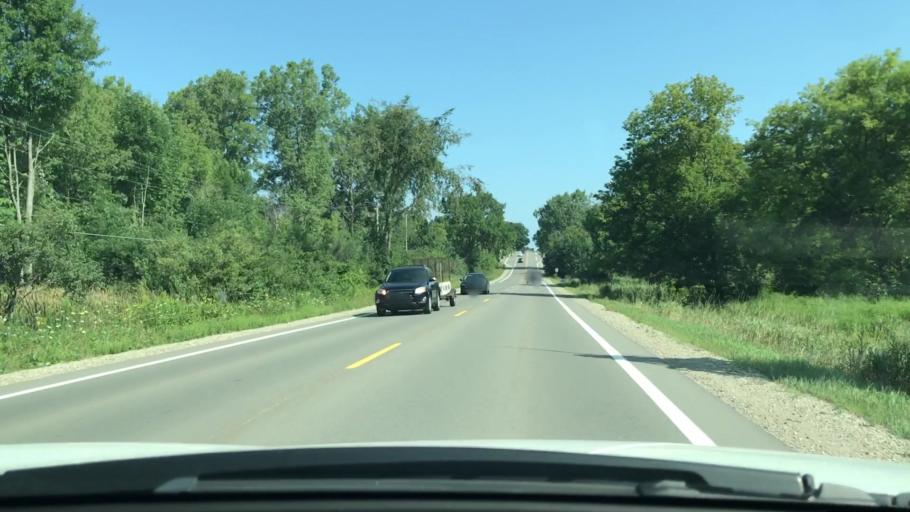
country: US
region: Michigan
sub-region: Oakland County
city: Oxford
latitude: 42.8040
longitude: -83.3334
